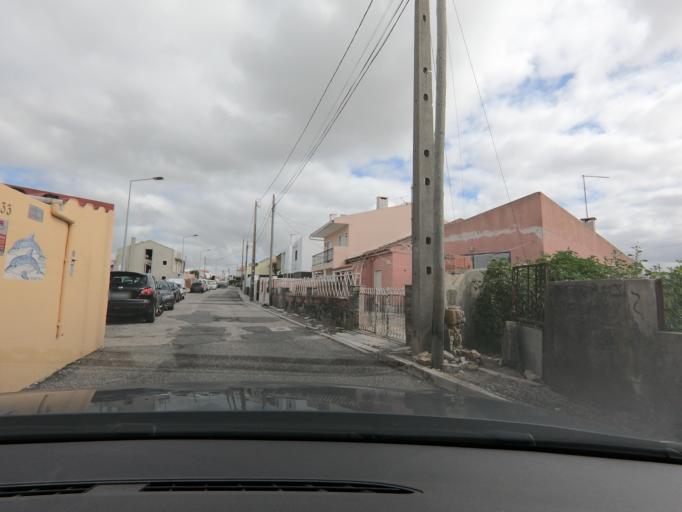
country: PT
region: Lisbon
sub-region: Cascais
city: Sao Domingos de Rana
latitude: 38.7182
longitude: -9.3459
